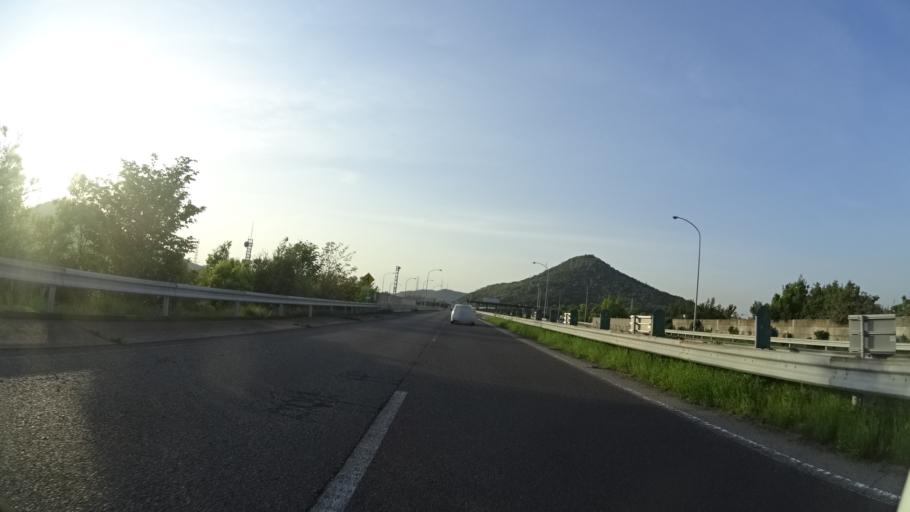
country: JP
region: Kagawa
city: Sakaidecho
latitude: 34.2954
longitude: 133.8449
